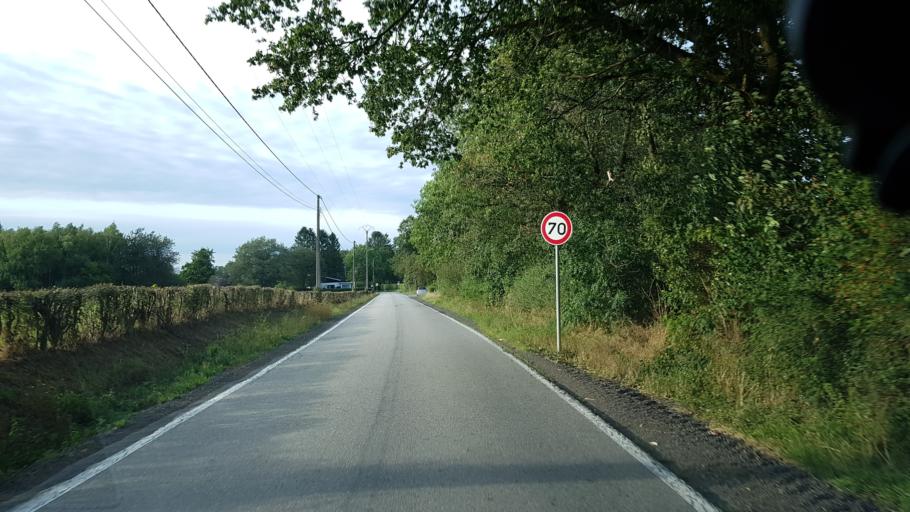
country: BE
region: Wallonia
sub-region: Province de Liege
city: Theux
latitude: 50.4958
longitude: 5.7704
